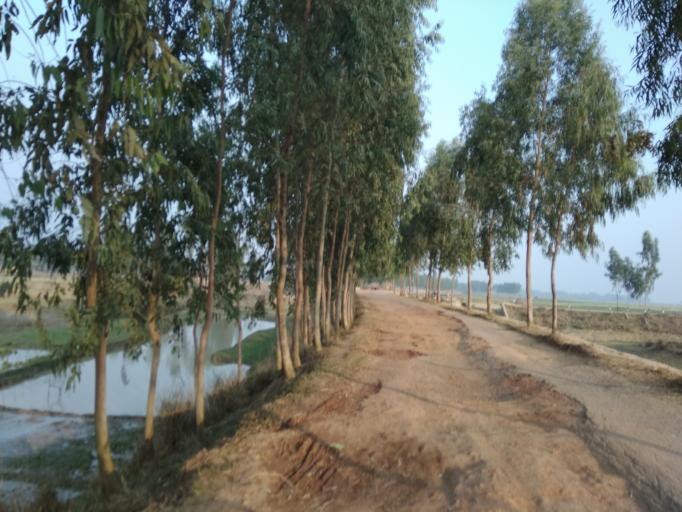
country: BD
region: Rajshahi
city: Bogra
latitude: 24.4761
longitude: 89.2691
